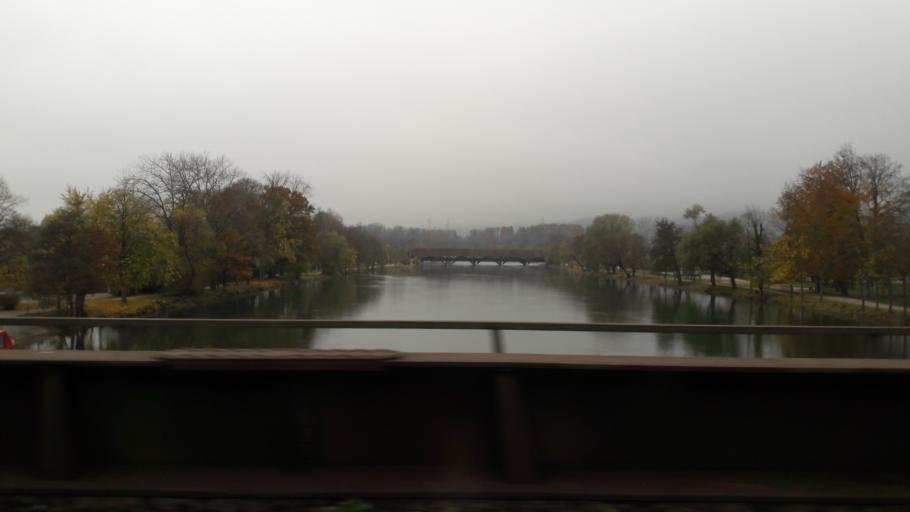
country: CH
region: Bern
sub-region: Oberaargau
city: Wangen an der Aare
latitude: 47.2354
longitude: 7.6606
